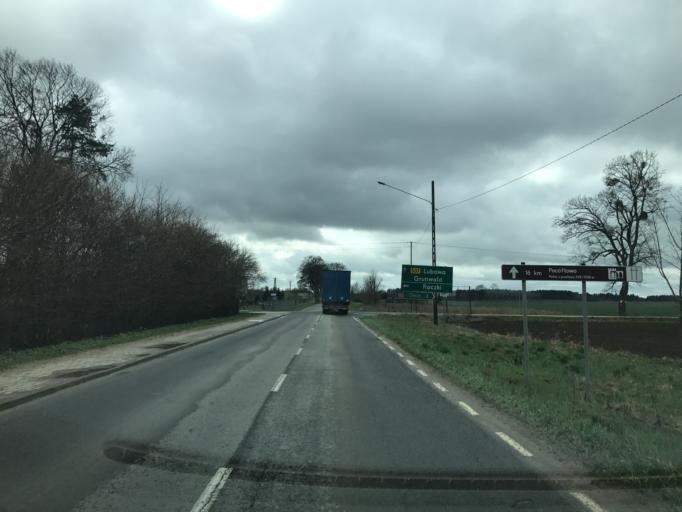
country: PL
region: Warmian-Masurian Voivodeship
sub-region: Powiat ostrodzki
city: Gierzwald
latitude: 53.5136
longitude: 20.1944
